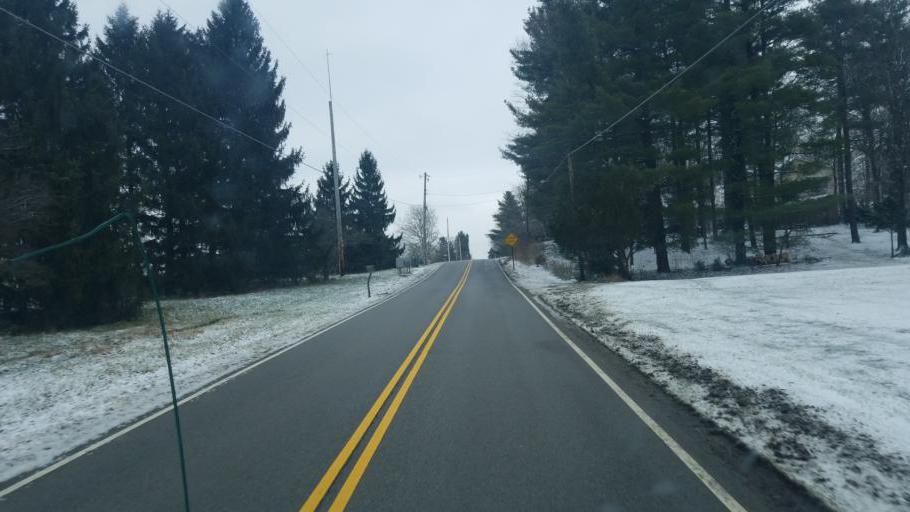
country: US
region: Ohio
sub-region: Franklin County
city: New Albany
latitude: 40.0428
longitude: -82.8308
